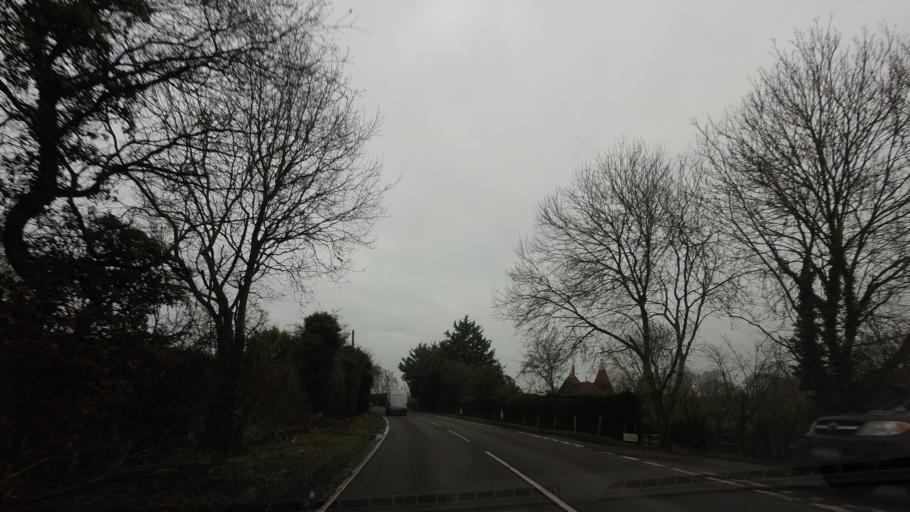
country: GB
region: England
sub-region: Kent
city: Staplehurst
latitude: 51.1329
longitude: 0.5593
